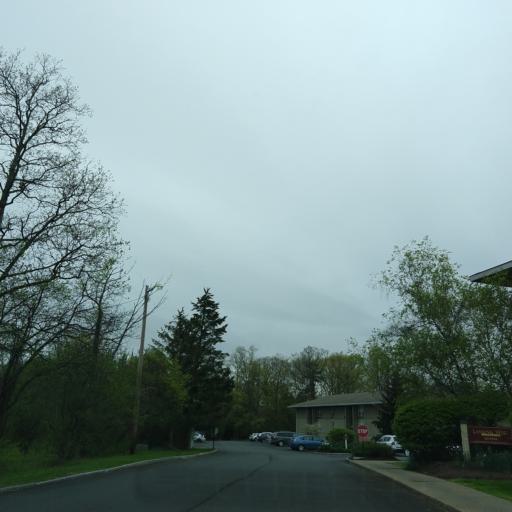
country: US
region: New York
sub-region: Tompkins County
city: Lansing
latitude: 42.4779
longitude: -76.4850
